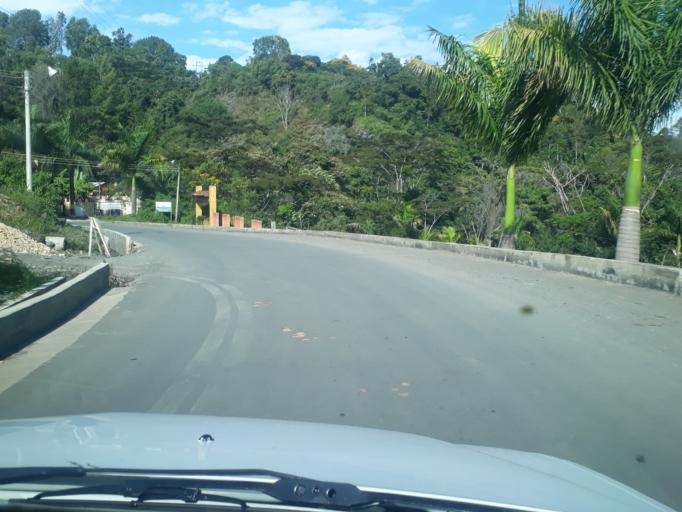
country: CO
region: Santander
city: Velez
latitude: 6.0594
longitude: -73.6402
